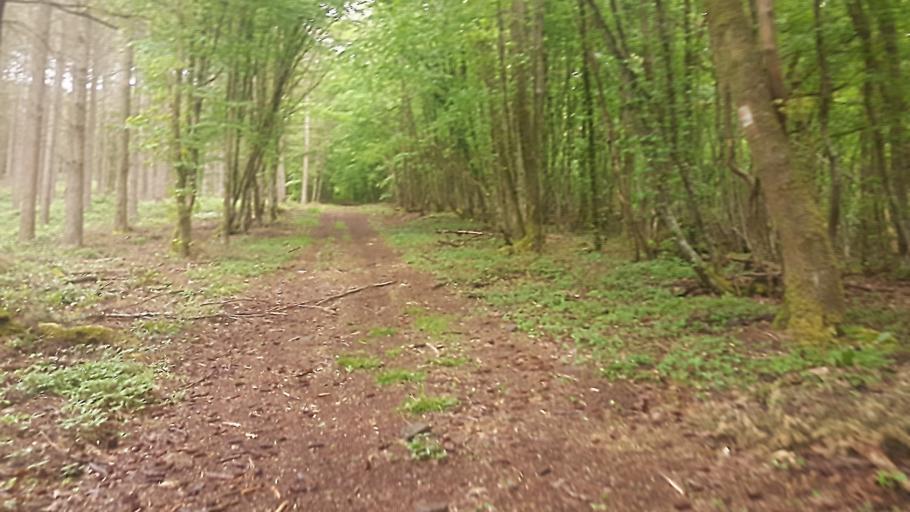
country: FR
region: Champagne-Ardenne
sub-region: Departement des Ardennes
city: Haybes
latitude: 50.0564
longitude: 4.6283
